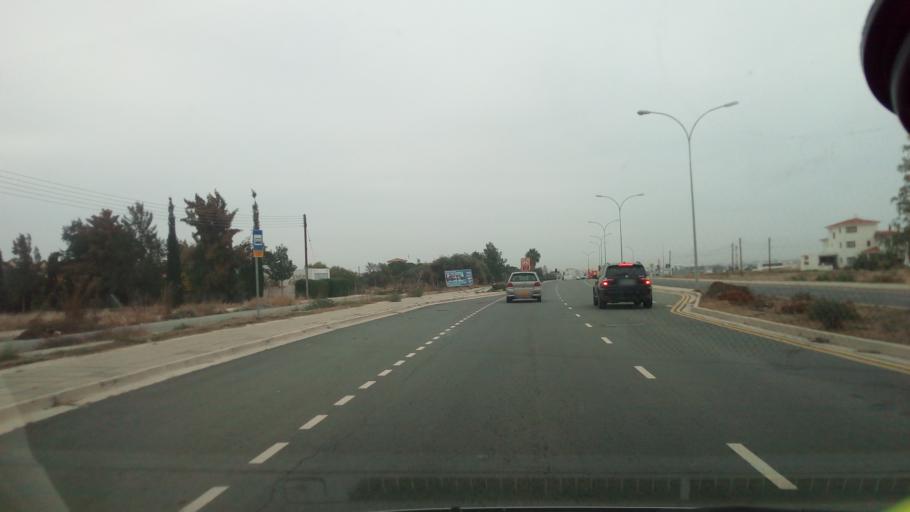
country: CY
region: Larnaka
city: Dhromolaxia
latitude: 34.9100
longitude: 33.5846
